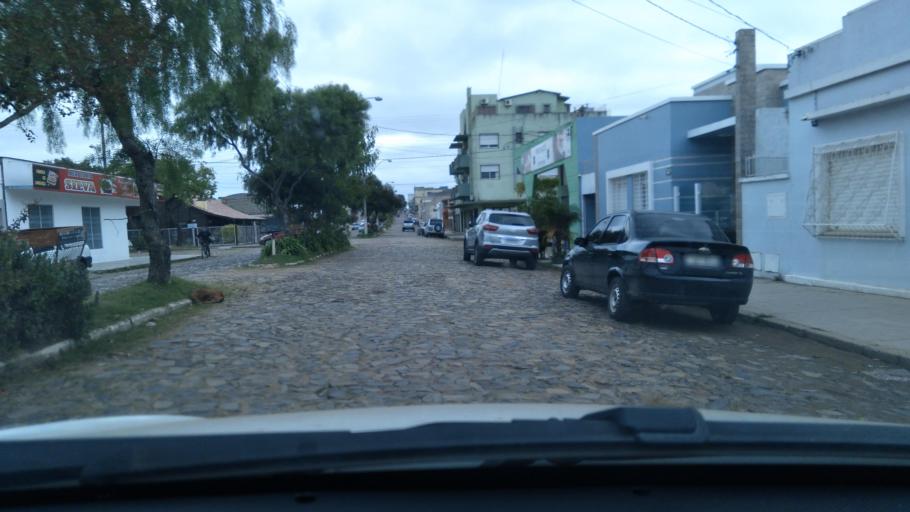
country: BR
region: Rio Grande do Sul
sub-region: Dom Pedrito
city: Dom Pedrito
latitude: -30.9858
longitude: -54.6682
